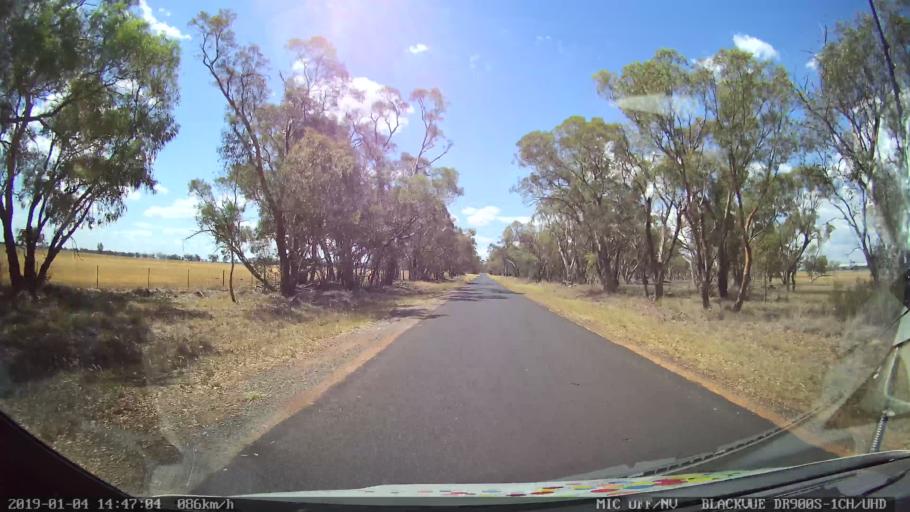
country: AU
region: New South Wales
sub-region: Dubbo Municipality
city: Dubbo
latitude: -32.0737
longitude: 148.6595
